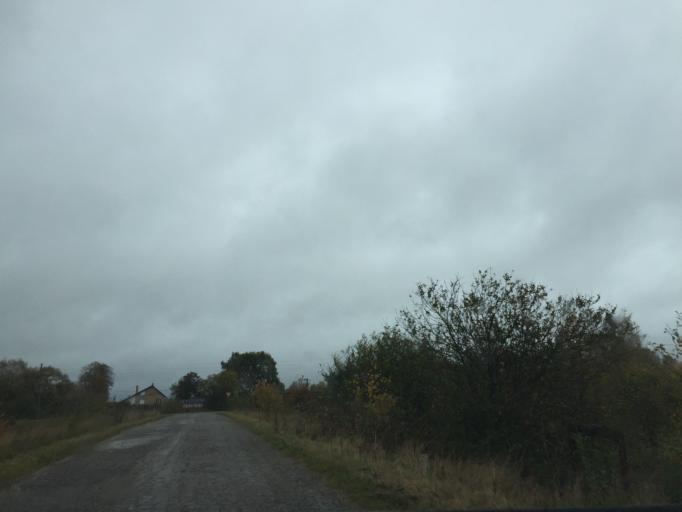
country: LV
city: Tireli
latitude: 56.8053
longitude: 23.5880
